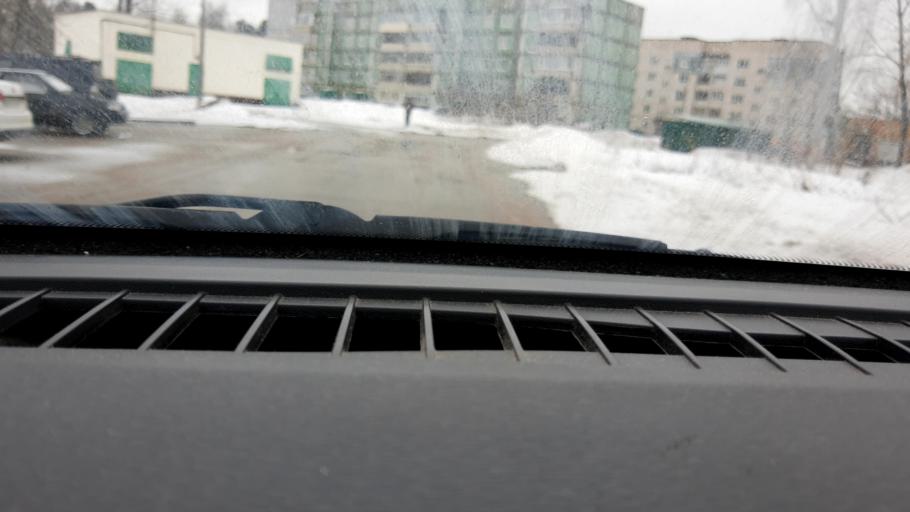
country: RU
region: Nizjnij Novgorod
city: Bor
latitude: 56.3312
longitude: 44.1089
